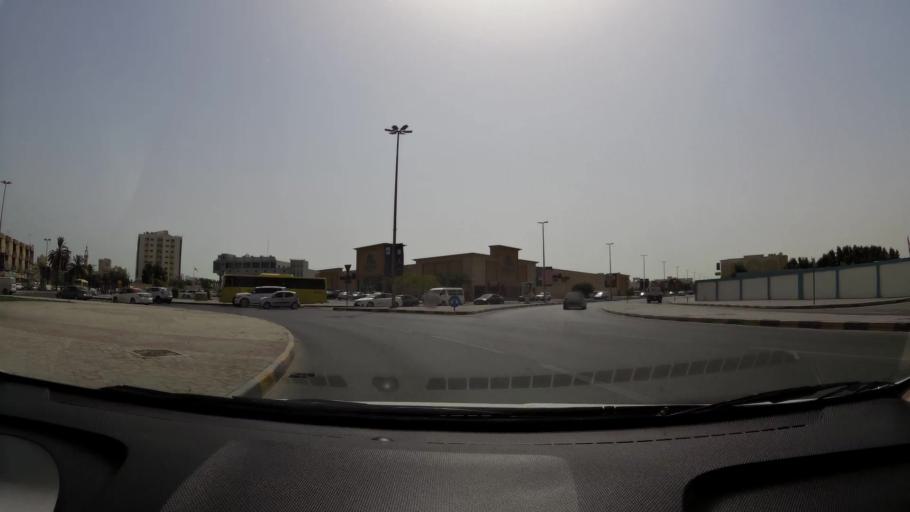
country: AE
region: Ash Shariqah
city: Sharjah
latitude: 25.3656
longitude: 55.4016
